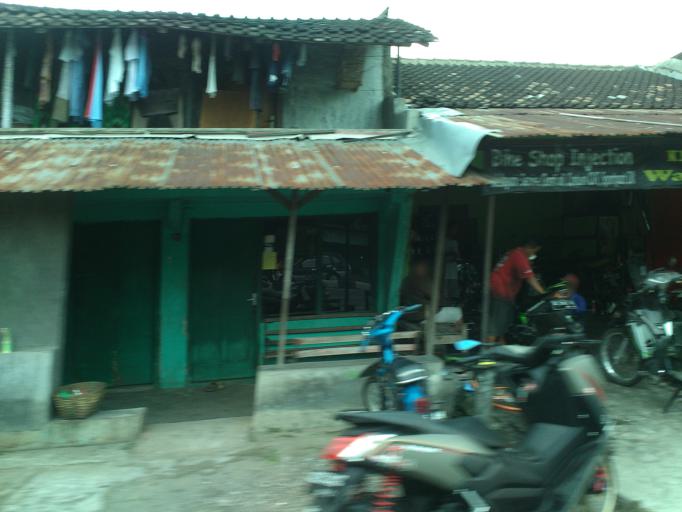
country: ID
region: Central Java
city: Ceper
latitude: -7.6594
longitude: 110.6752
